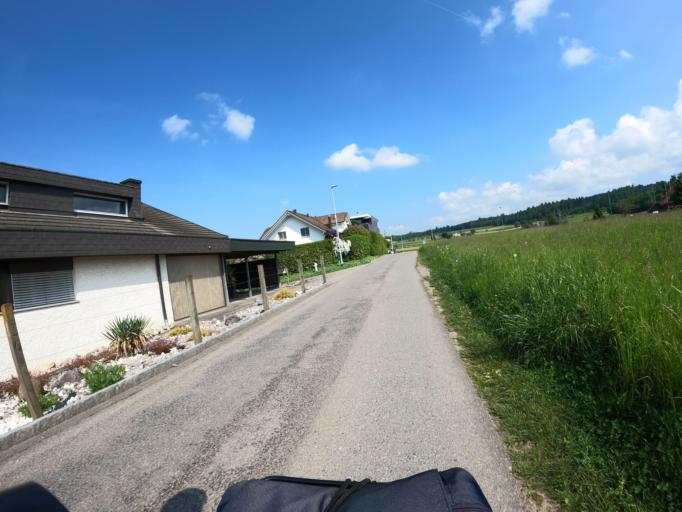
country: CH
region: Zug
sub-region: Zug
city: Steinhausen
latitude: 47.1968
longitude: 8.4939
